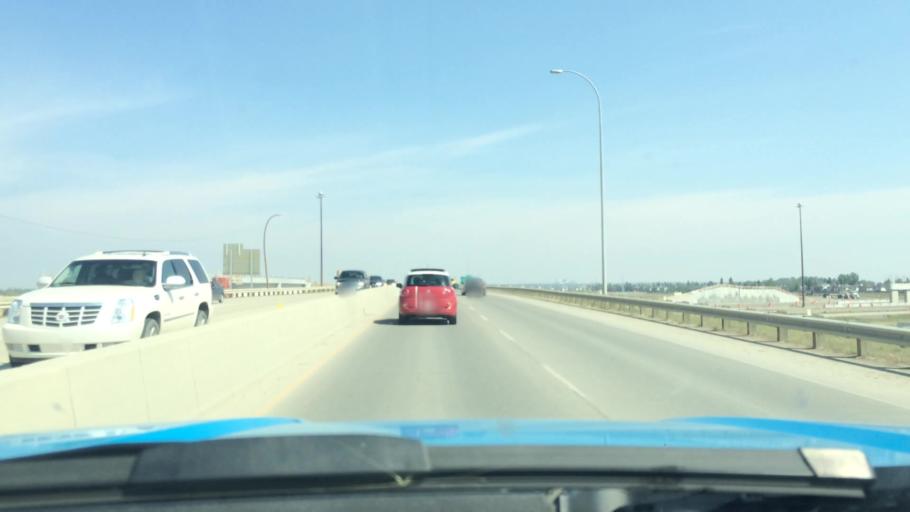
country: CA
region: Alberta
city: Calgary
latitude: 50.8926
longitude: -114.0573
